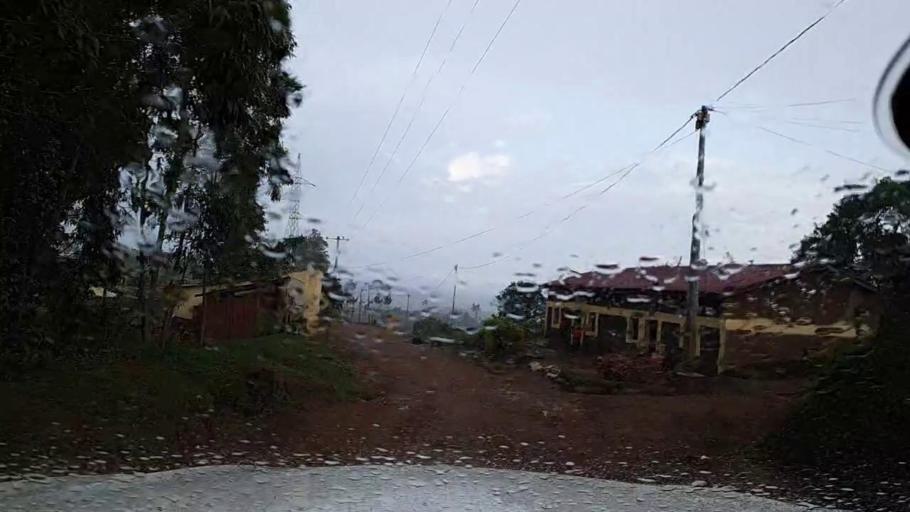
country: BI
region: Kayanza
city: Kayanza
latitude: -2.7811
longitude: 29.5349
